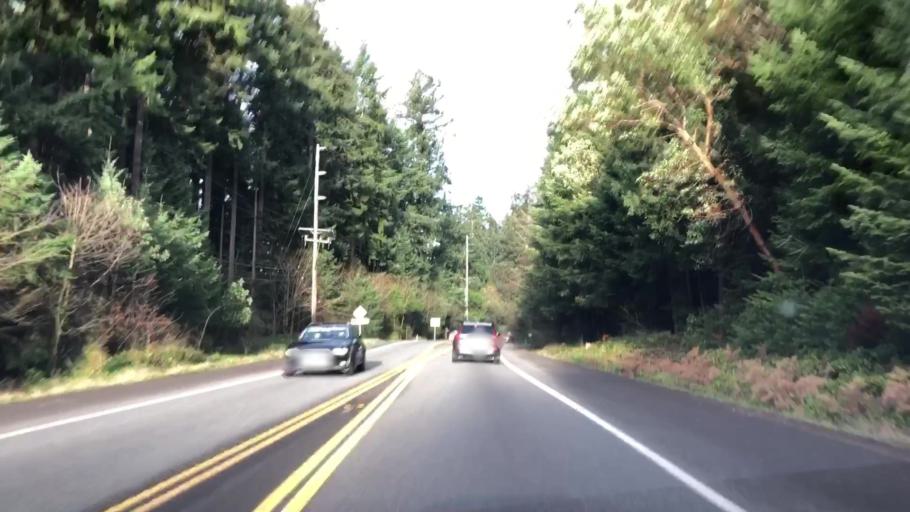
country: US
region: Washington
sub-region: Kitsap County
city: Suquamish
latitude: 47.7045
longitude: -122.5594
